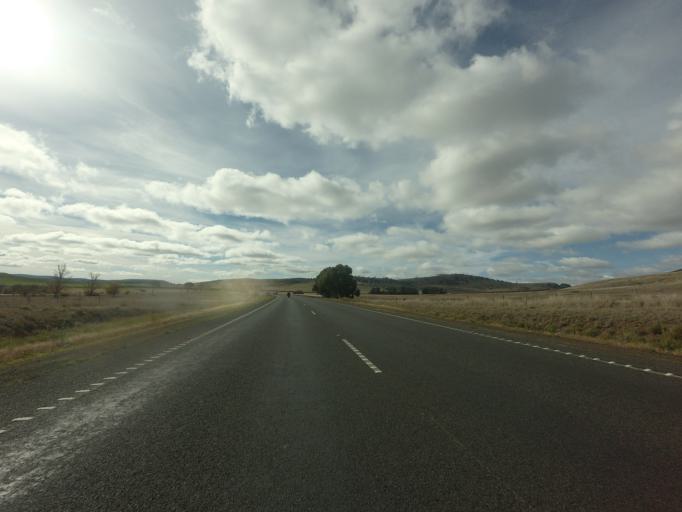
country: AU
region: Tasmania
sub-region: Brighton
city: Bridgewater
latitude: -42.3716
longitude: 147.3321
